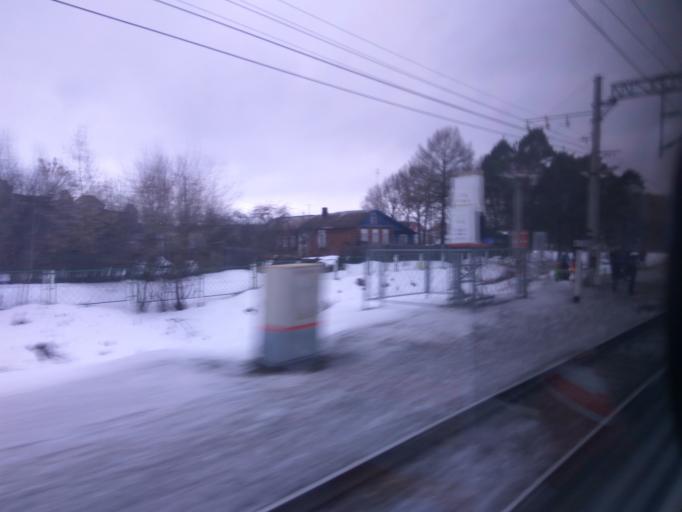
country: RU
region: Tverskaya
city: Tver
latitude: 56.8680
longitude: 35.8389
